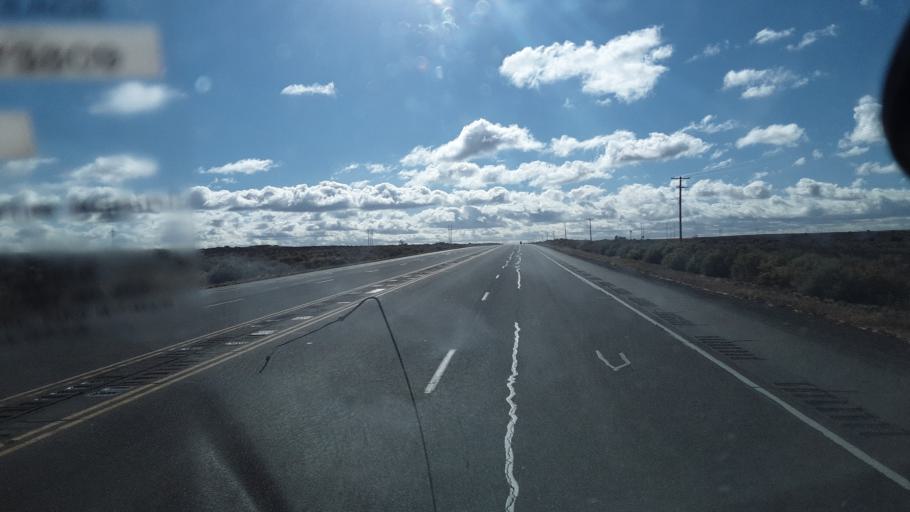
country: US
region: New Mexico
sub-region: San Juan County
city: Lee Acres
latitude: 36.5885
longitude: -108.0028
